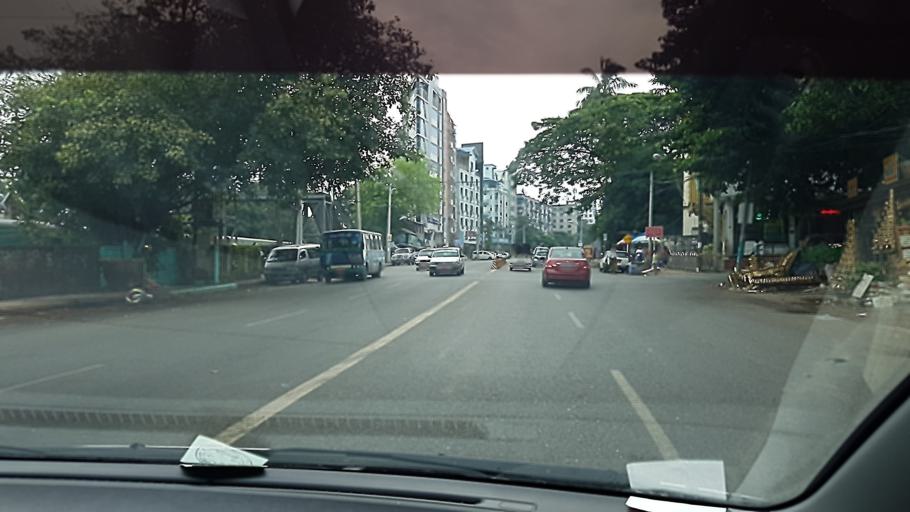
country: MM
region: Yangon
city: Yangon
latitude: 16.8011
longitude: 96.1260
